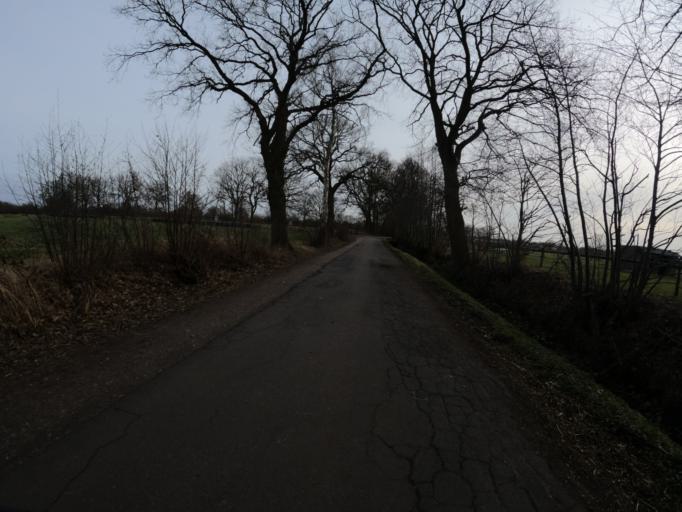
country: DE
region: Schleswig-Holstein
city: Rellingen
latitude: 53.5952
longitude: 9.7973
